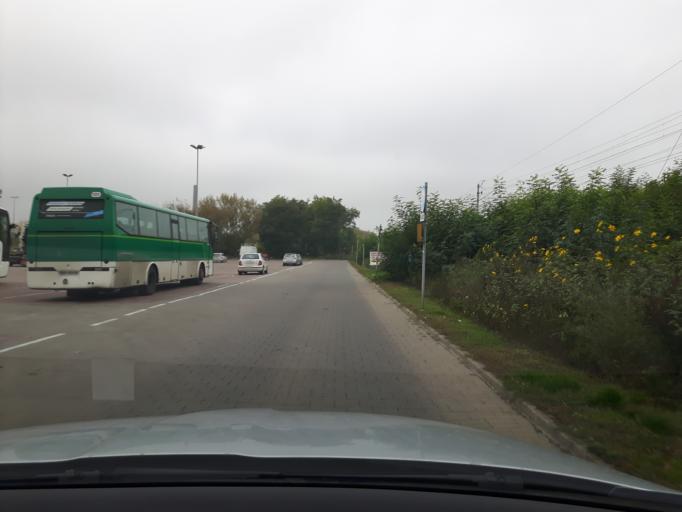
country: PL
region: Masovian Voivodeship
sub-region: Warszawa
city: Praga Polnoc
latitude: 52.2642
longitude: 21.0511
